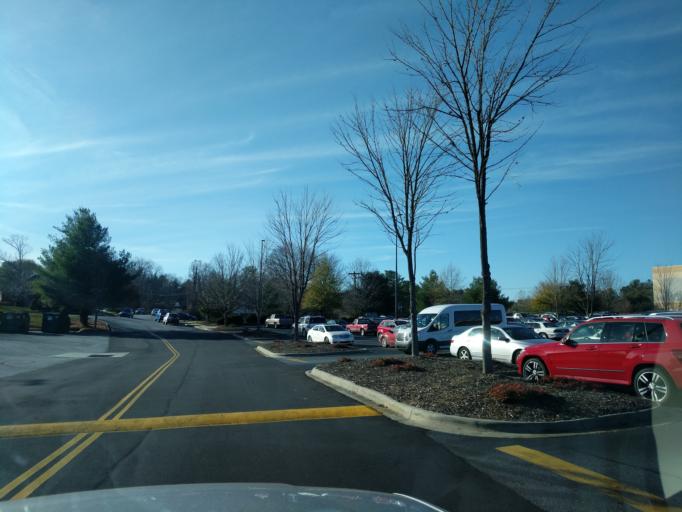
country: US
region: North Carolina
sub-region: Henderson County
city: Hendersonville
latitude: 35.3385
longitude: -82.4458
